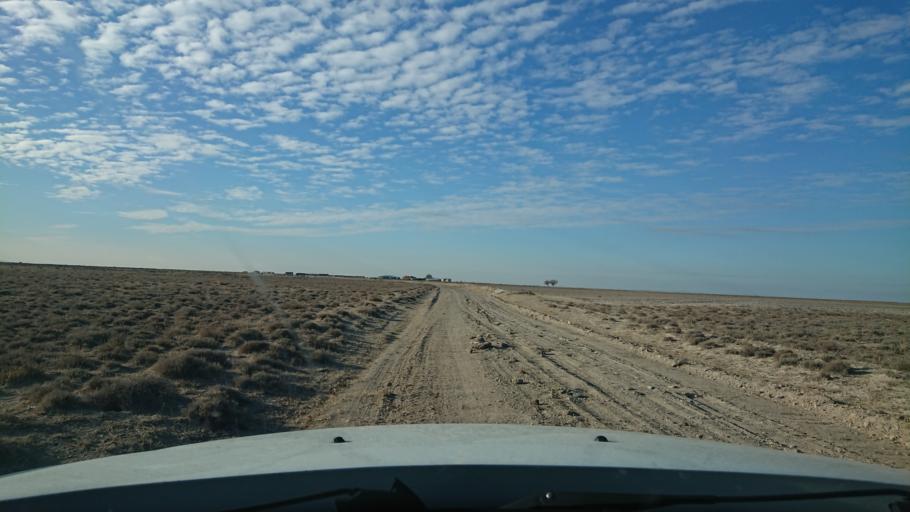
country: TR
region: Aksaray
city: Eskil
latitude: 38.5643
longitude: 33.3036
